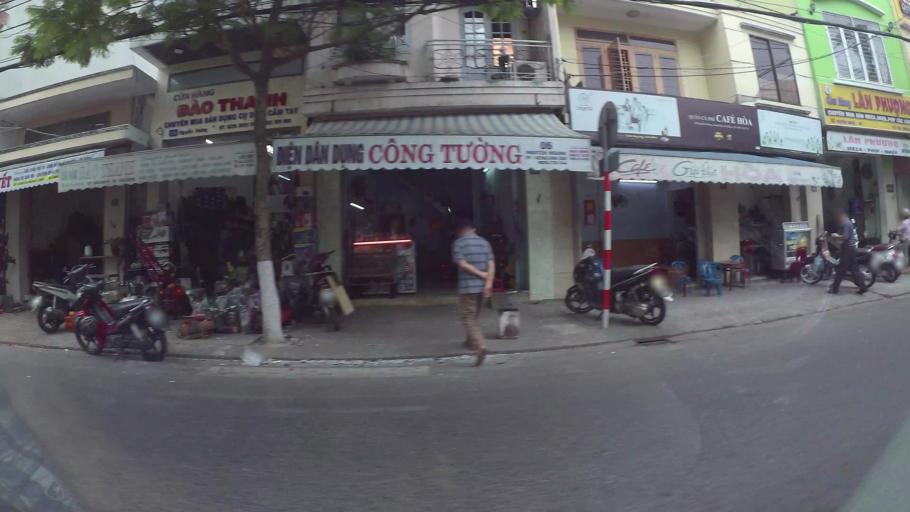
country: VN
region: Da Nang
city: Da Nang
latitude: 16.0652
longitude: 108.2145
